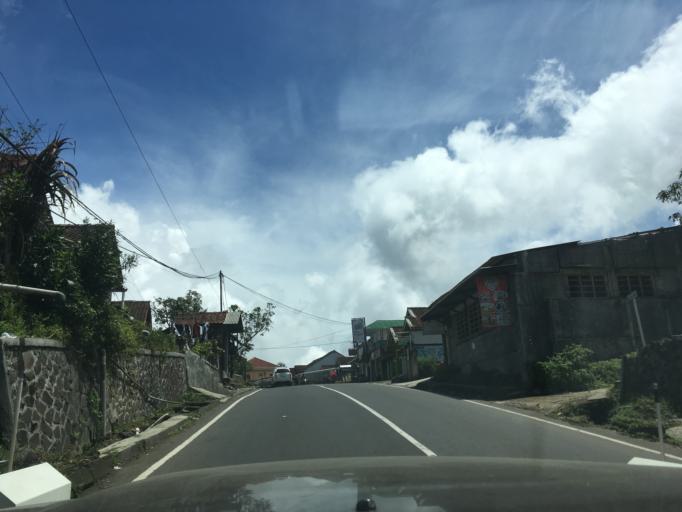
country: ID
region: West Java
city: Lembang
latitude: -6.7903
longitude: 107.6544
